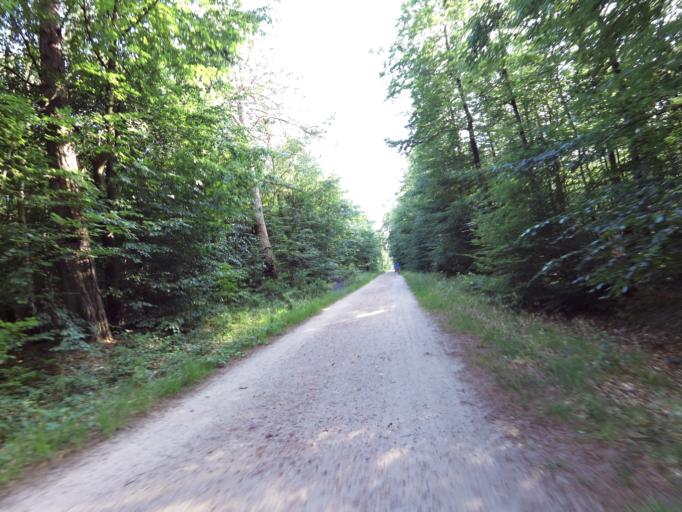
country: DE
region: Lower Saxony
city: Nordholz
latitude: 53.8477
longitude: 8.5939
